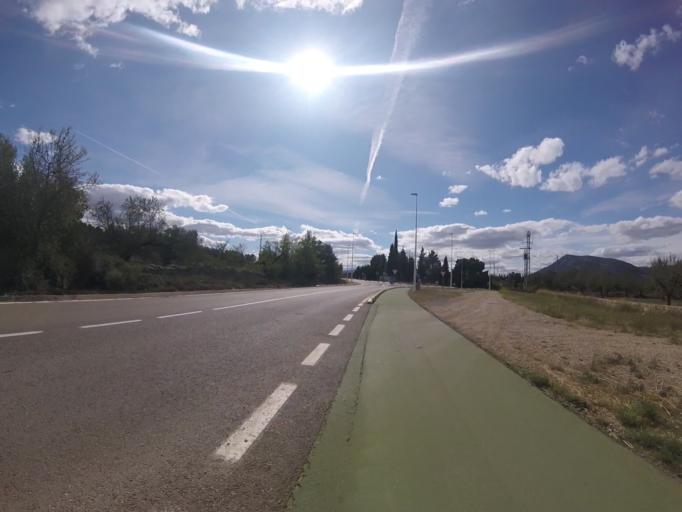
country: ES
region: Valencia
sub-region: Provincia de Castello
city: Cati
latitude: 40.4172
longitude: 0.0717
